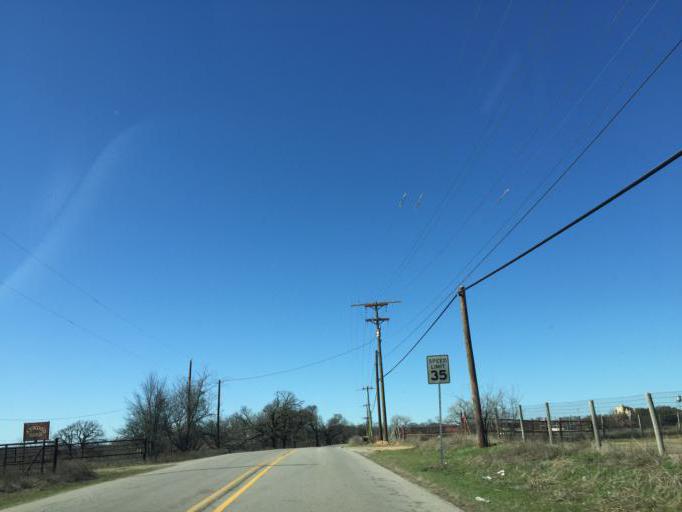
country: US
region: Texas
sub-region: Parker County
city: Hudson Oaks
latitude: 32.7446
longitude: -97.7494
